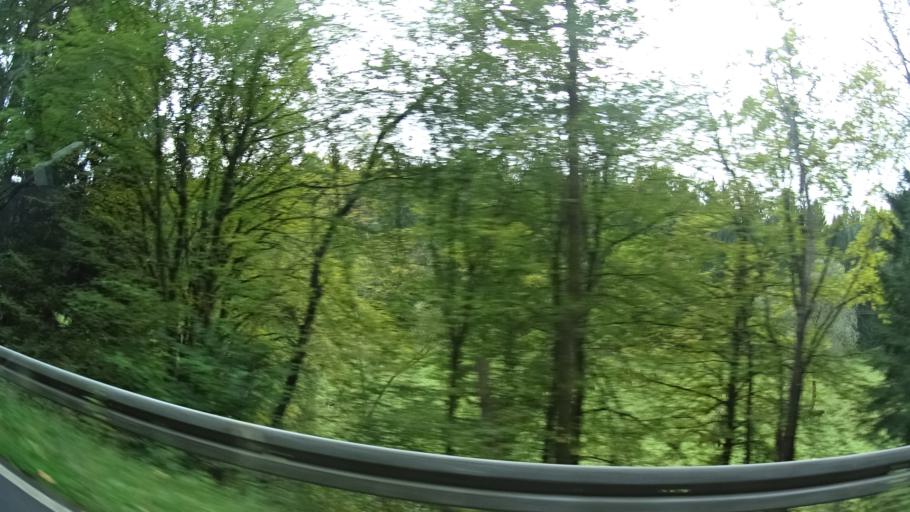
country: DE
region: Bavaria
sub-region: Regierungsbezirk Unterfranken
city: Kirchzell
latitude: 49.6120
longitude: 9.1468
